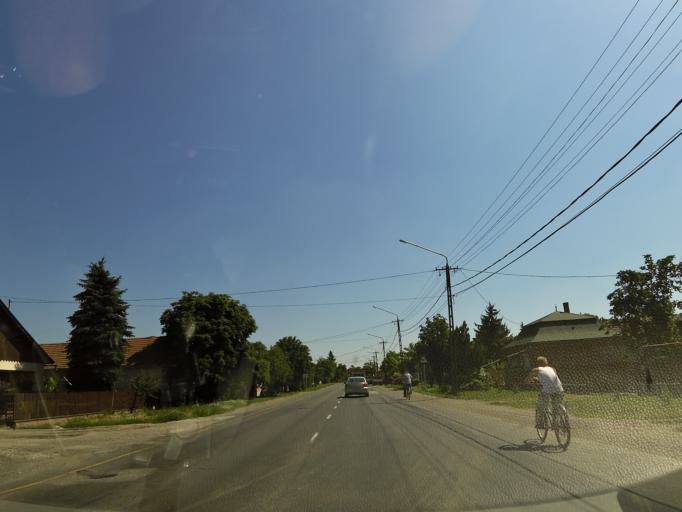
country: HU
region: Jasz-Nagykun-Szolnok
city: Fegyvernek
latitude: 47.2344
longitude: 20.5270
